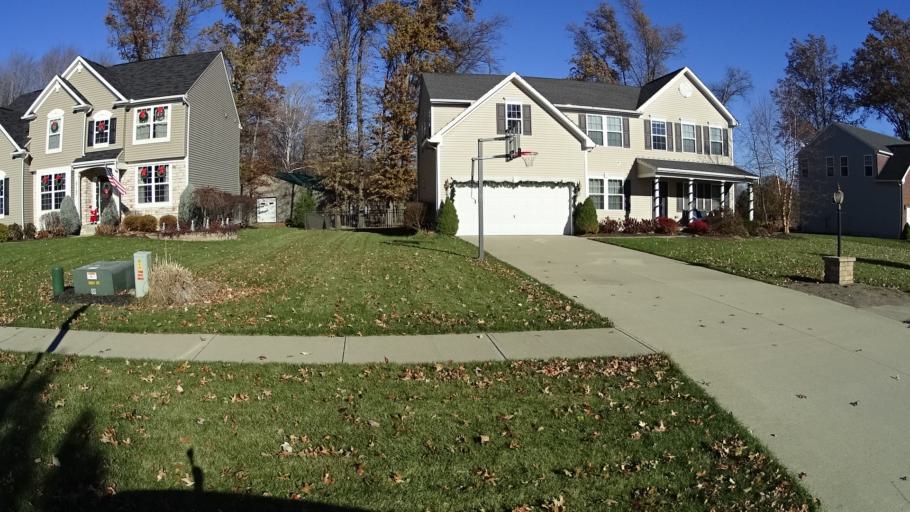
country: US
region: Ohio
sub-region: Lorain County
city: Avon
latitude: 41.4373
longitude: -82.0371
